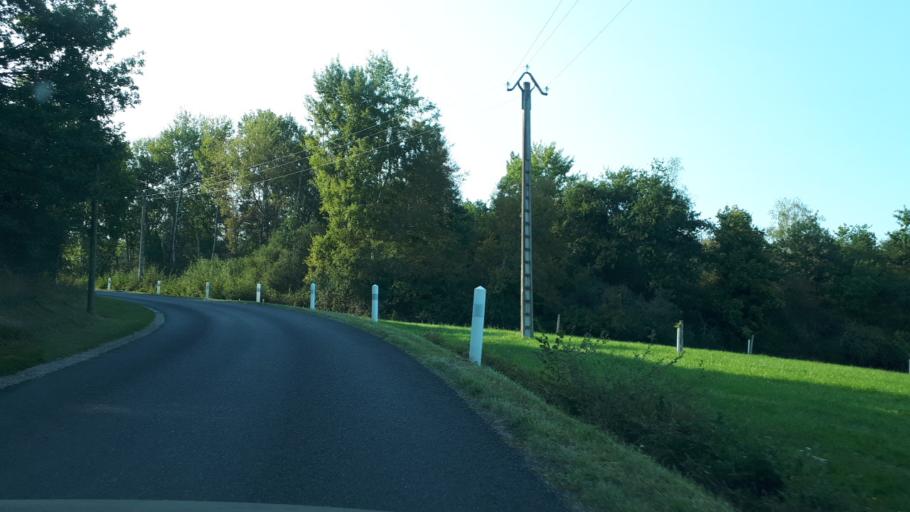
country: FR
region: Centre
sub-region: Departement du Cher
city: Vasselay
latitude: 47.2165
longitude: 2.3697
